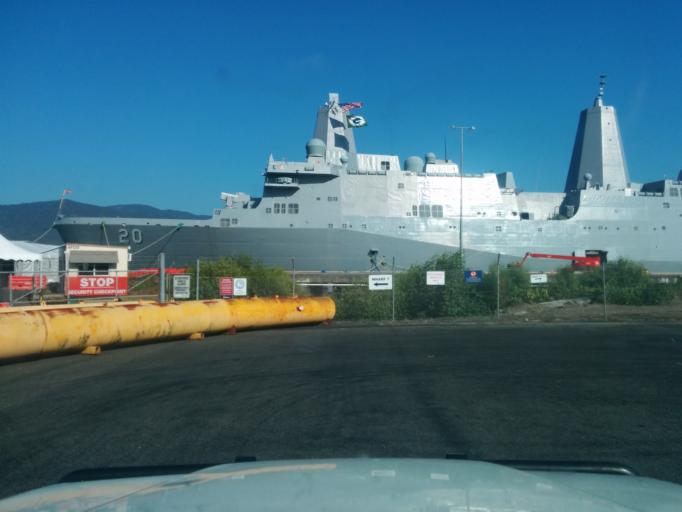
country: AU
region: Queensland
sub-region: Cairns
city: Cairns
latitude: -16.9307
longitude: 145.7790
